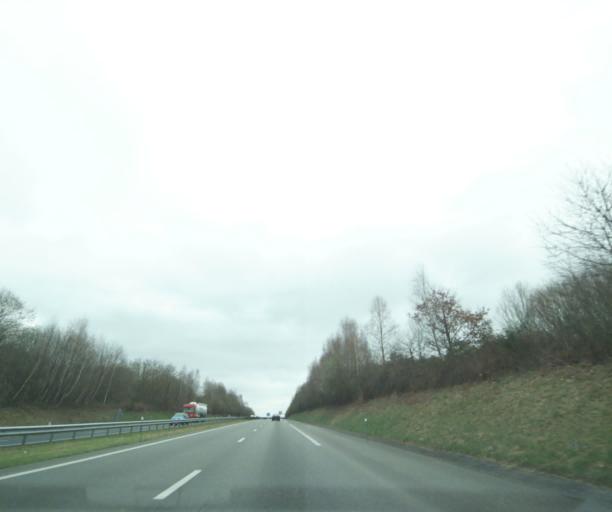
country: FR
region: Limousin
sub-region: Departement de la Correze
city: Uzerche
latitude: 45.4003
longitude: 1.5636
